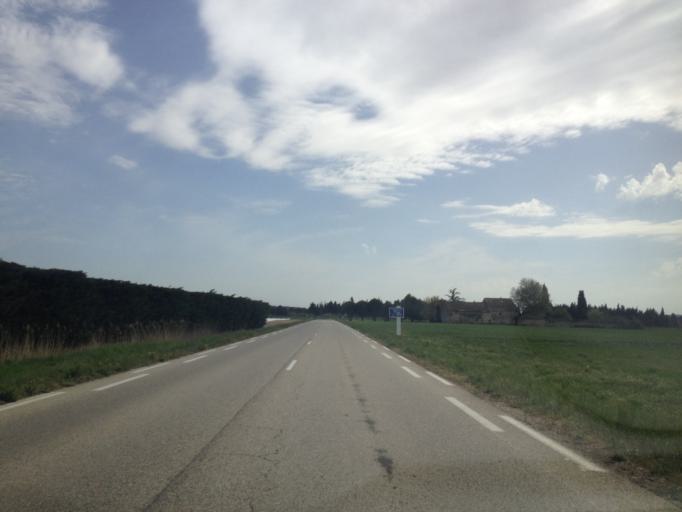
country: FR
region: Provence-Alpes-Cote d'Azur
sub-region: Departement du Vaucluse
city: Orange
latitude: 44.1270
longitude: 4.7829
